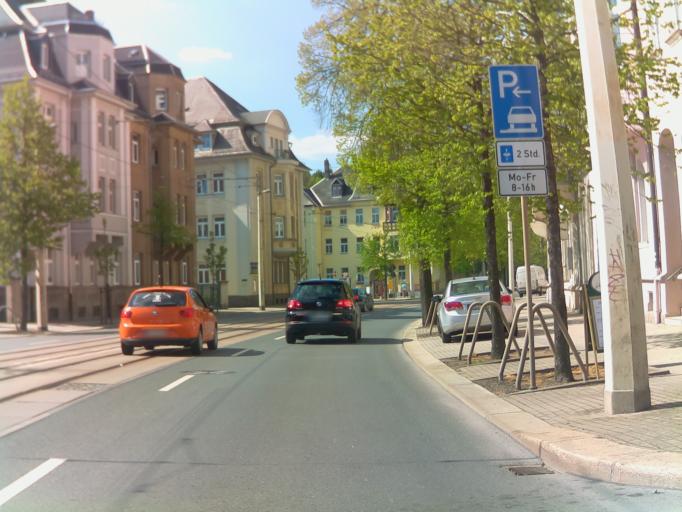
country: DE
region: Saxony
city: Plauen
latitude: 50.5133
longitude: 12.1217
